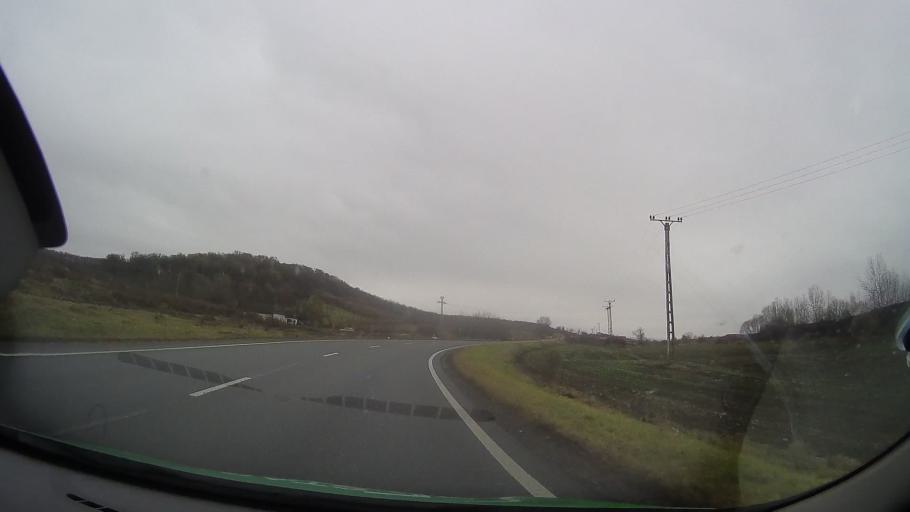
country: RO
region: Mures
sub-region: Comuna Breaza
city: Breaza
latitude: 46.7802
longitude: 24.6550
